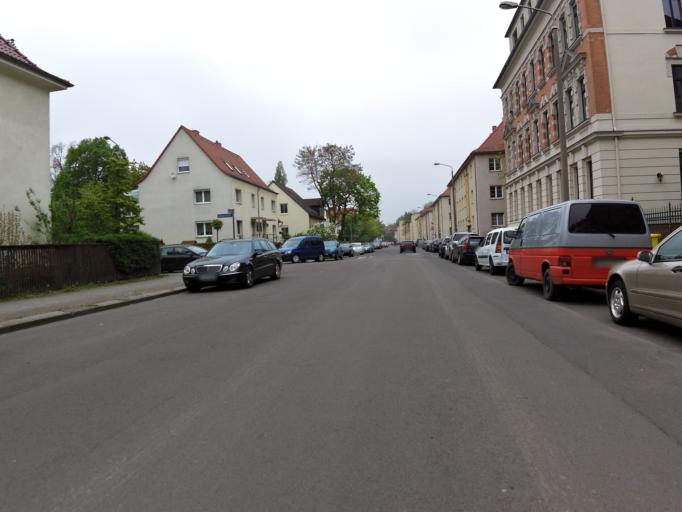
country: DE
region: Saxony
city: Leipzig
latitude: 51.3628
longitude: 12.3797
